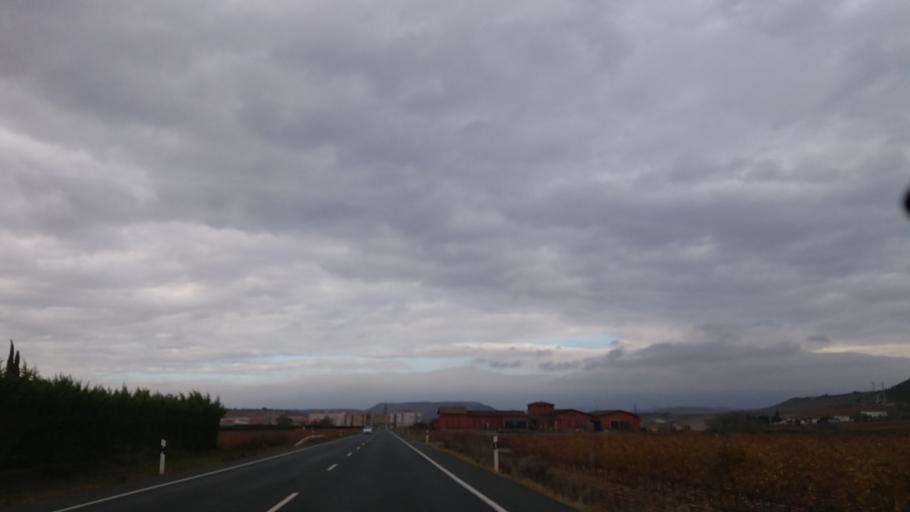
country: ES
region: La Rioja
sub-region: Provincia de La Rioja
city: Fuenmayor
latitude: 42.4572
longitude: -2.5546
